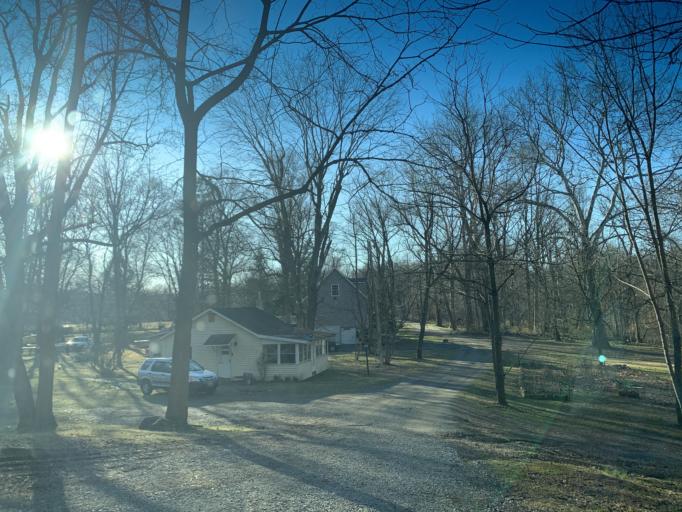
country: US
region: Maryland
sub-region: Cecil County
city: Rising Sun
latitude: 39.6593
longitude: -76.1538
